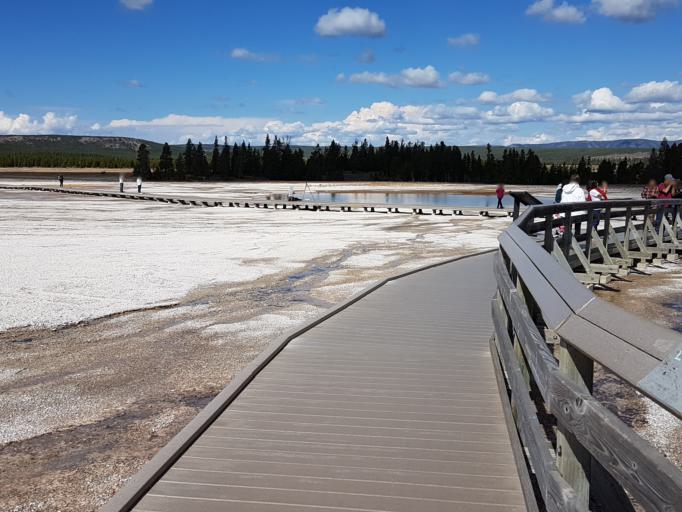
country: US
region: Montana
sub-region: Gallatin County
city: West Yellowstone
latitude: 44.5262
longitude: -110.8373
